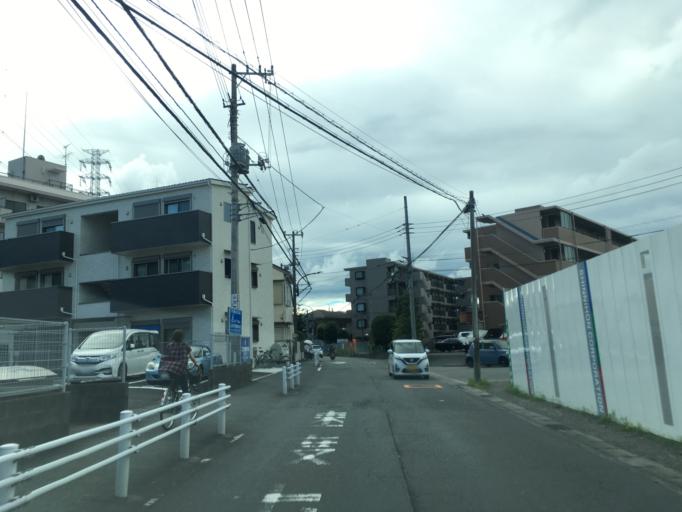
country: JP
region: Tokyo
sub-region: Machida-shi
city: Machida
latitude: 35.5567
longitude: 139.4171
